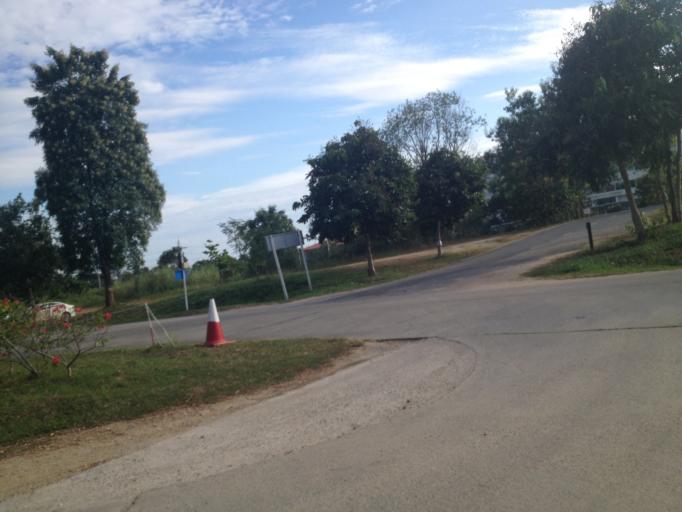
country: TH
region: Chiang Mai
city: Chiang Mai
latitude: 18.7587
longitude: 98.9400
